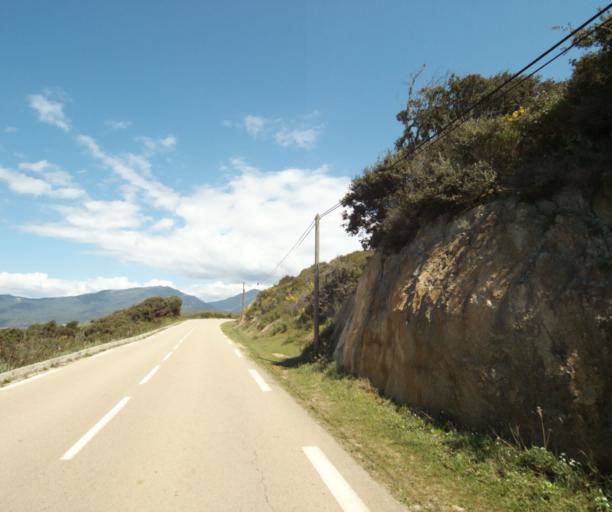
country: FR
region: Corsica
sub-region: Departement de la Corse-du-Sud
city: Propriano
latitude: 41.6511
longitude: 8.8804
